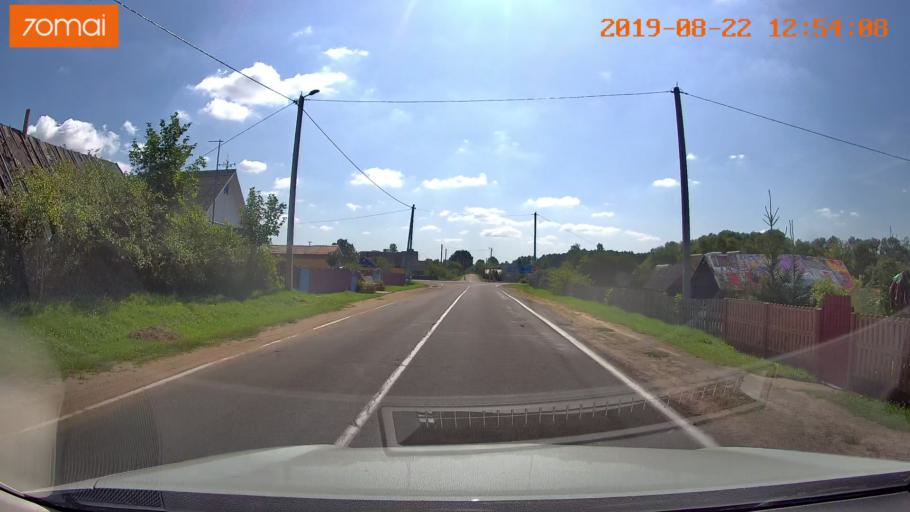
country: BY
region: Minsk
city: Prawdzinski
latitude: 53.4386
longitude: 27.6930
